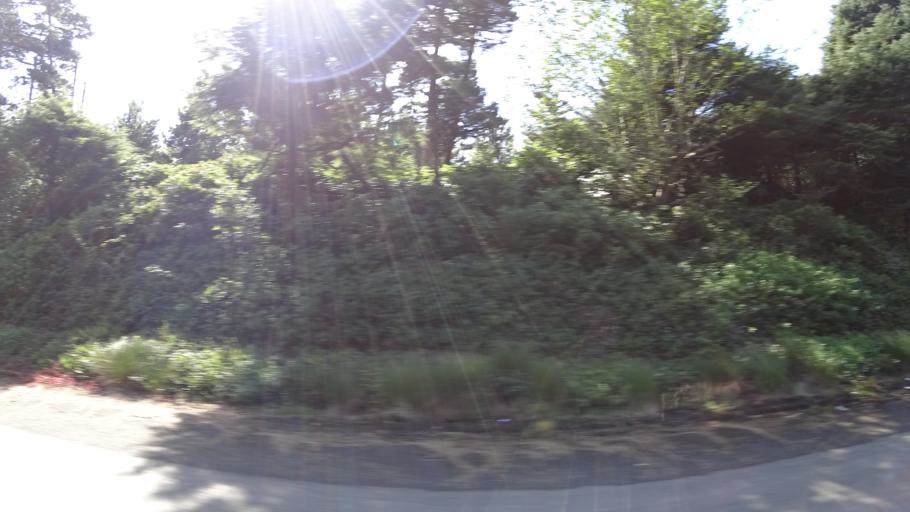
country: US
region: Oregon
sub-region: Lincoln County
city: Newport
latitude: 44.6840
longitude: -124.0635
